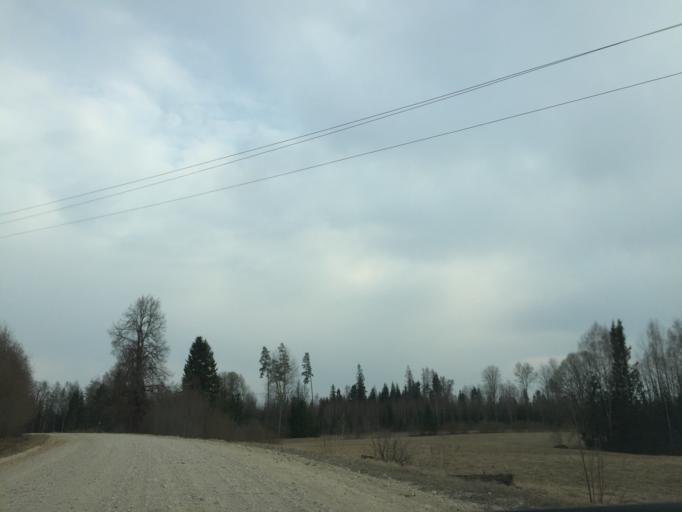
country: LV
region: Priekuli
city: Priekuli
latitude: 57.2110
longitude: 25.4144
